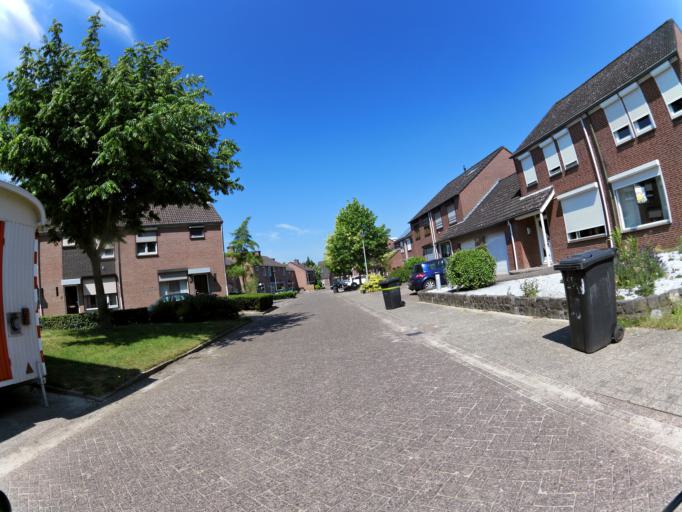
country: NL
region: Limburg
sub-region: Gemeente Kerkrade
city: Kerkrade
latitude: 50.9183
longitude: 6.0457
